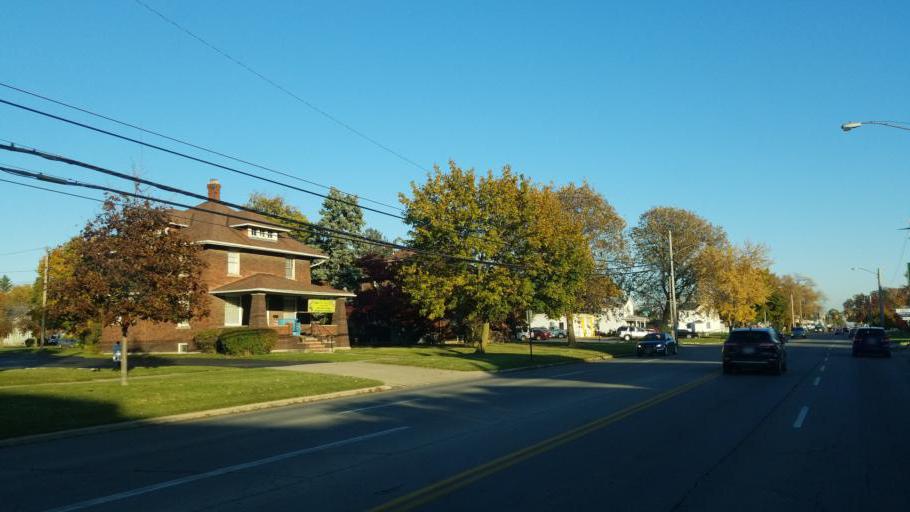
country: US
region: Ohio
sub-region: Sandusky County
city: Fremont
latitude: 41.3438
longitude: -83.1000
